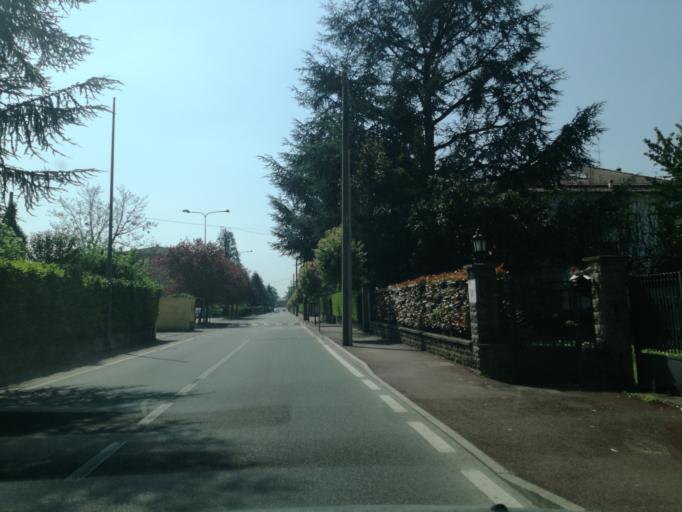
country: IT
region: Lombardy
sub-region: Provincia di Lecco
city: Robbiate
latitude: 45.6834
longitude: 9.4384
